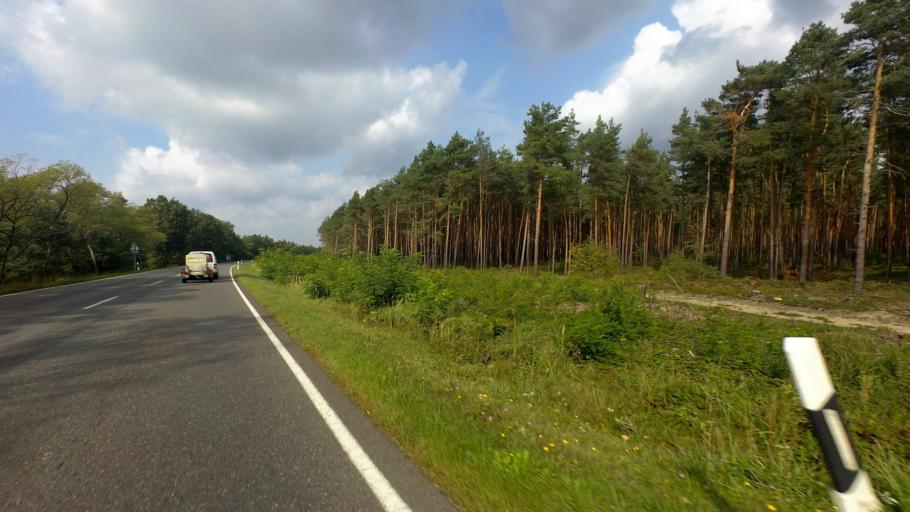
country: DE
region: Brandenburg
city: Elsterwerda
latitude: 51.4879
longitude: 13.4828
